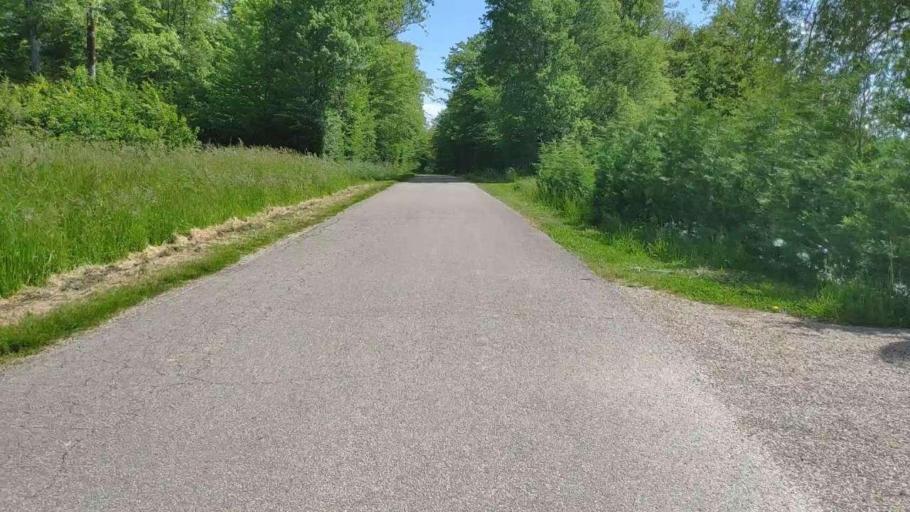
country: FR
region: Franche-Comte
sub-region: Departement du Jura
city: Bletterans
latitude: 46.7069
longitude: 5.4113
